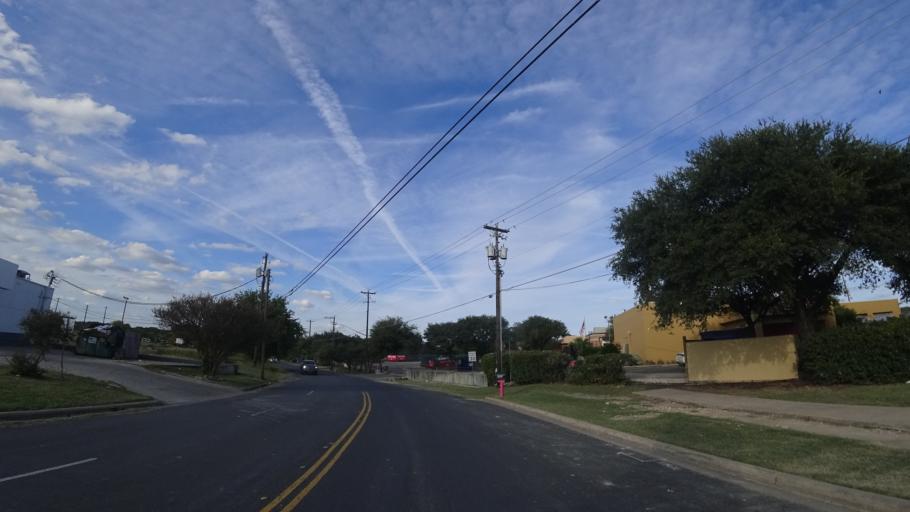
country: US
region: Texas
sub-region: Travis County
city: Onion Creek
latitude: 30.1911
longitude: -97.7715
